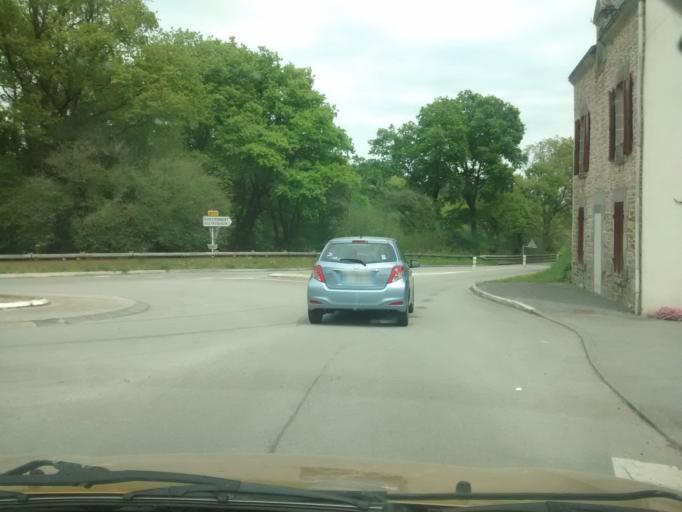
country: FR
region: Brittany
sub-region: Departement du Morbihan
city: Questembert
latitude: 47.6619
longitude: -2.4719
